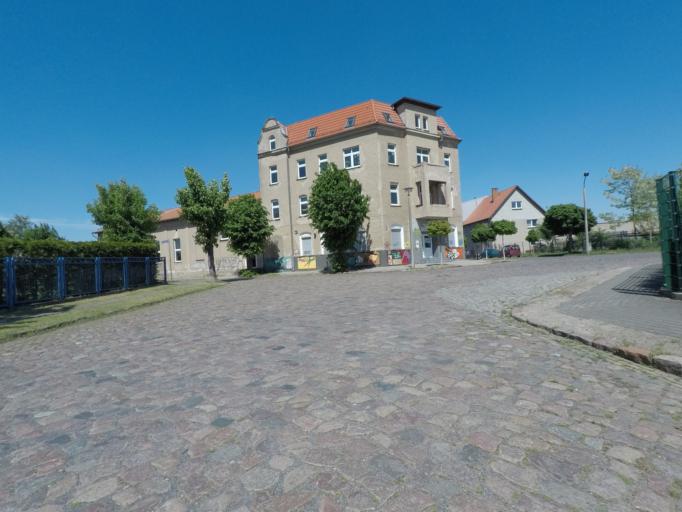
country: DE
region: Brandenburg
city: Melchow
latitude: 52.8343
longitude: 13.7321
